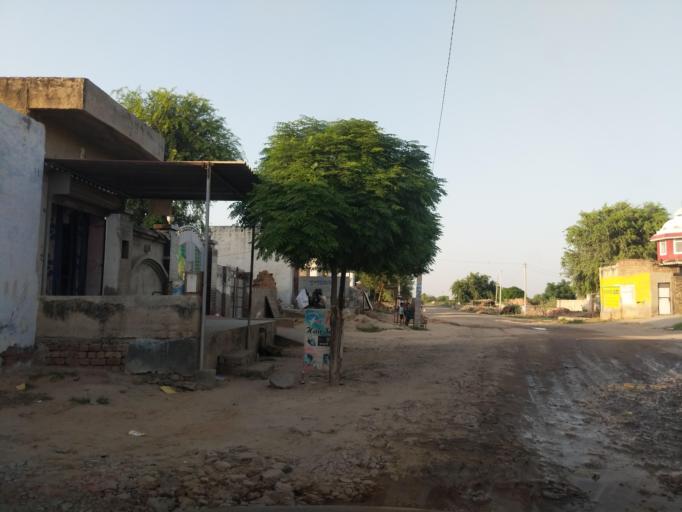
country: IN
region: Rajasthan
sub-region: Churu
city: Rajgarh
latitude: 28.5643
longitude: 75.3665
